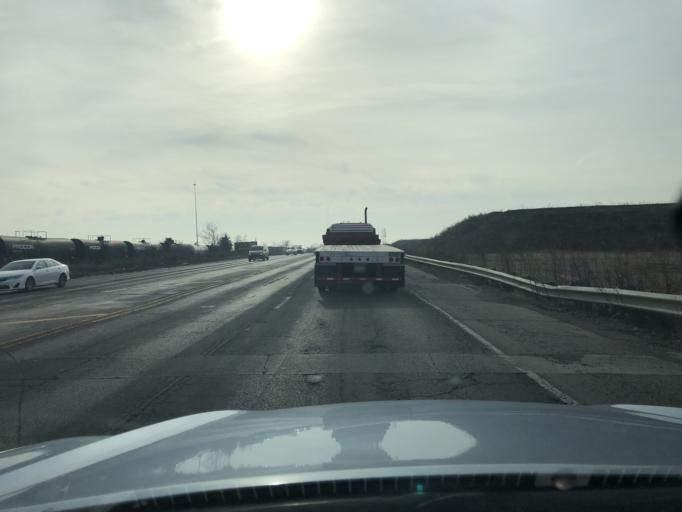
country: US
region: Illinois
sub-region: DuPage County
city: Bensenville
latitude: 41.9819
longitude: -87.9399
